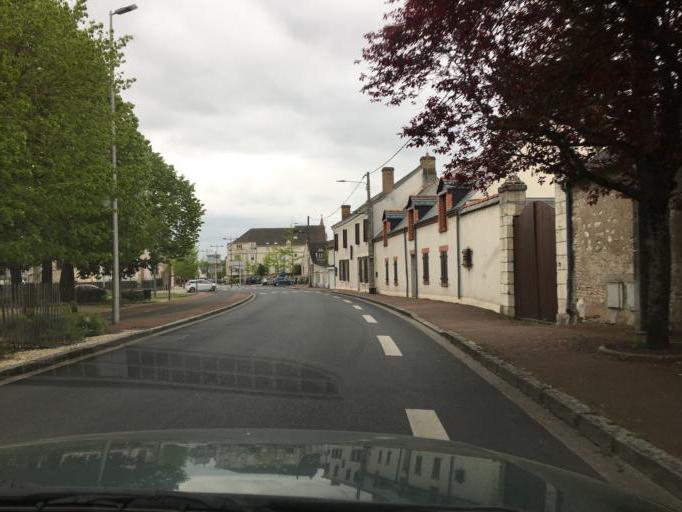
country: FR
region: Centre
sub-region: Departement du Loiret
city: Saint-Jean-de-la-Ruelle
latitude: 47.9168
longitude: 1.8747
